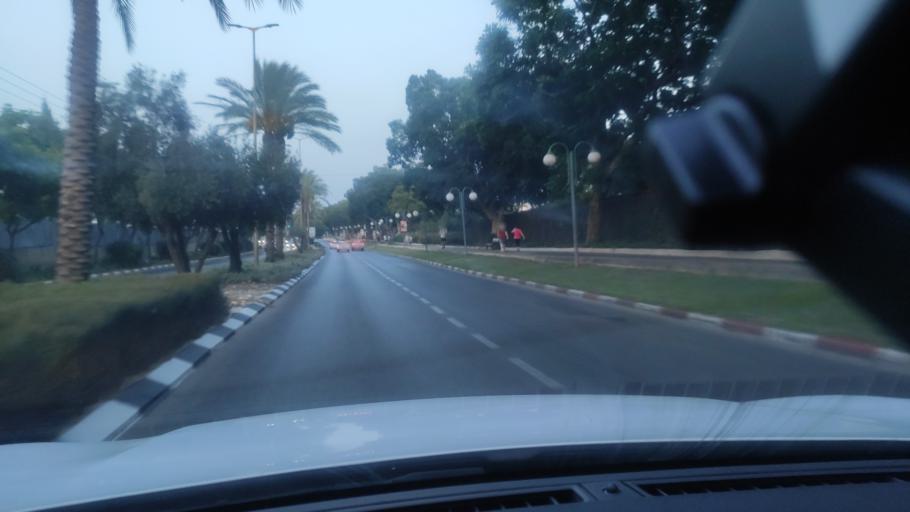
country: IL
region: Central District
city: Kfar Saba
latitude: 32.1830
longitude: 34.9247
